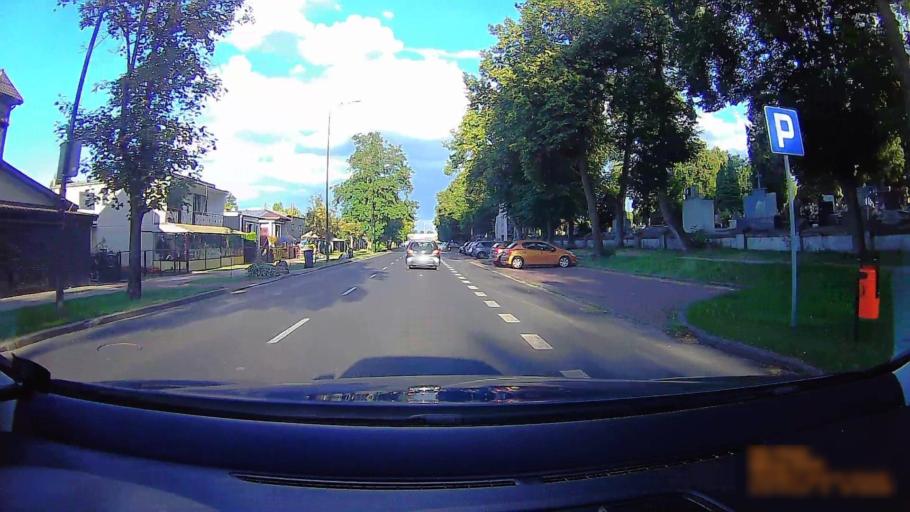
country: PL
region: Greater Poland Voivodeship
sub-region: Konin
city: Konin
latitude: 52.2036
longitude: 18.2664
